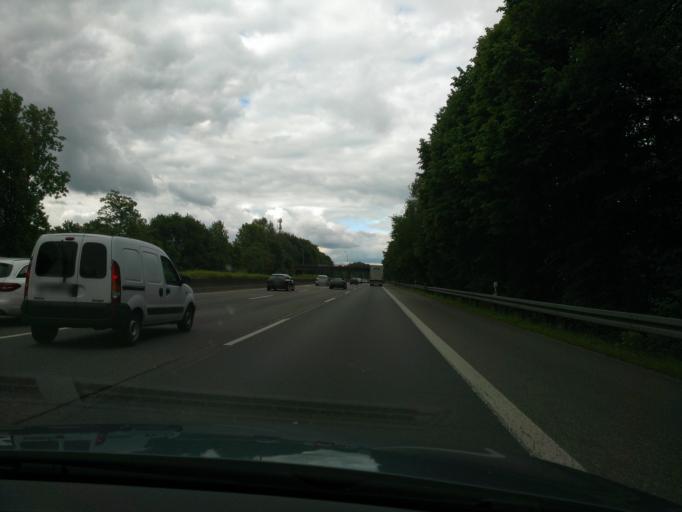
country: DE
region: North Rhine-Westphalia
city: Opladen
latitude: 51.0619
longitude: 7.0685
